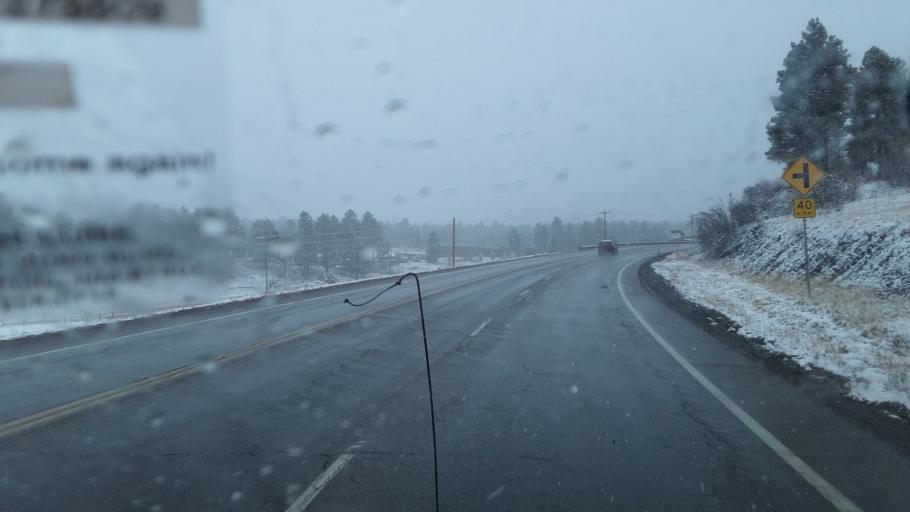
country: US
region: Colorado
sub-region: Archuleta County
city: Pagosa Springs
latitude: 37.2671
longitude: -107.0269
